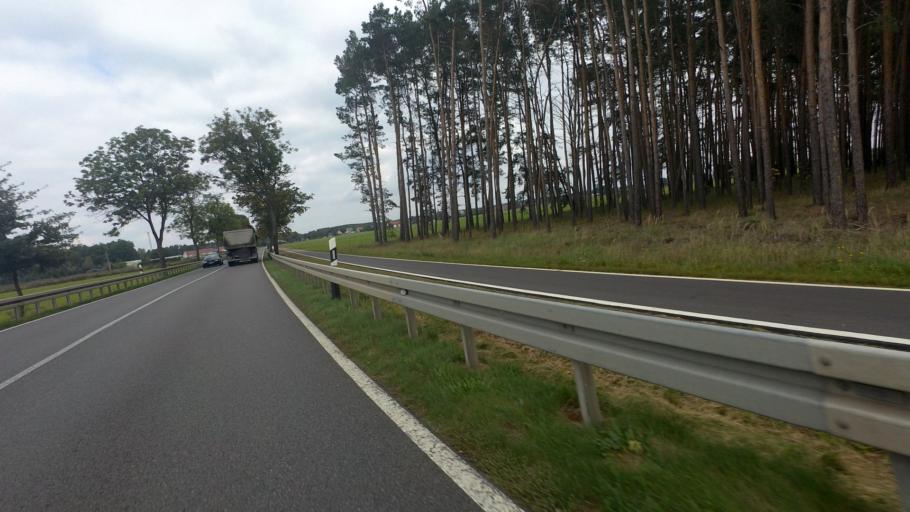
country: DE
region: Brandenburg
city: Schilda
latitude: 51.5704
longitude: 13.3600
